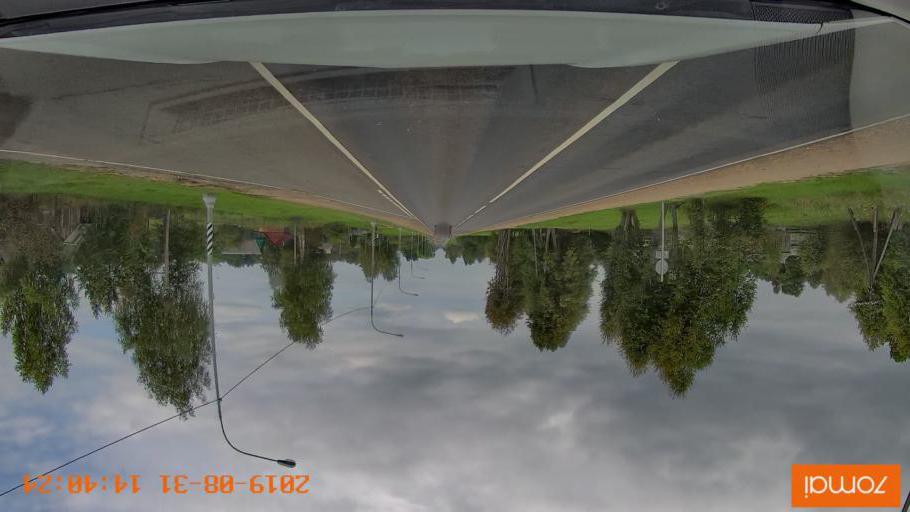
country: RU
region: Smolensk
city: Yekimovichi
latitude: 54.1970
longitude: 33.5708
